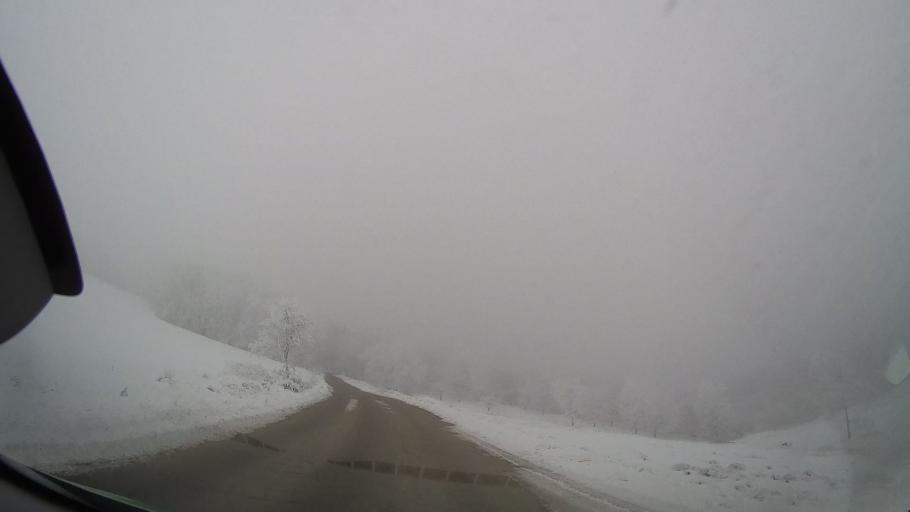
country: RO
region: Neamt
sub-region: Comuna Valea Ursului
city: Valea Ursului
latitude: 46.8362
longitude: 27.0709
